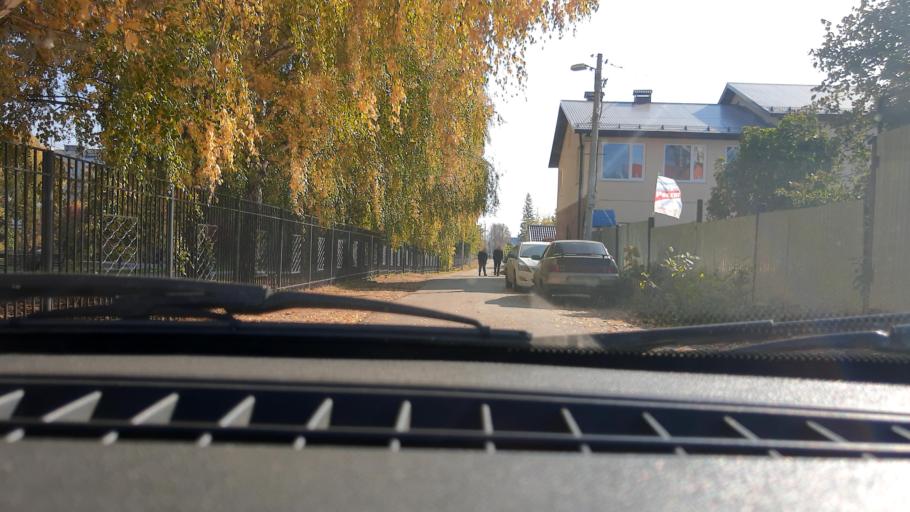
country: RU
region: Bashkortostan
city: Mikhaylovka
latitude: 54.7888
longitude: 55.8742
